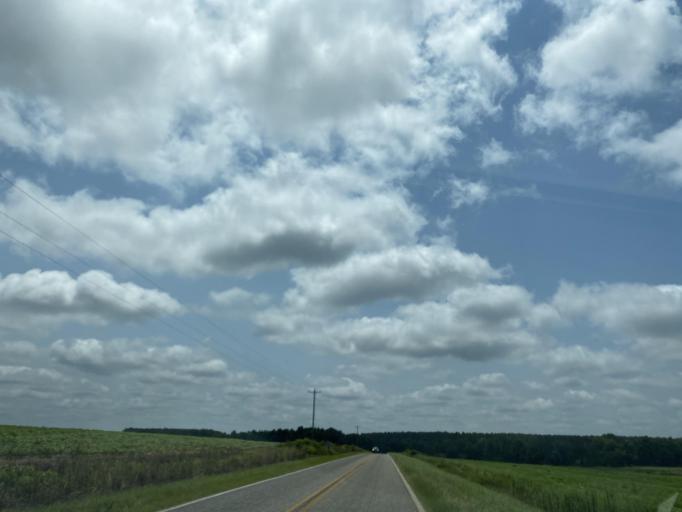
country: US
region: Georgia
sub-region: Wheeler County
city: Alamo
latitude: 32.0947
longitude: -82.7575
